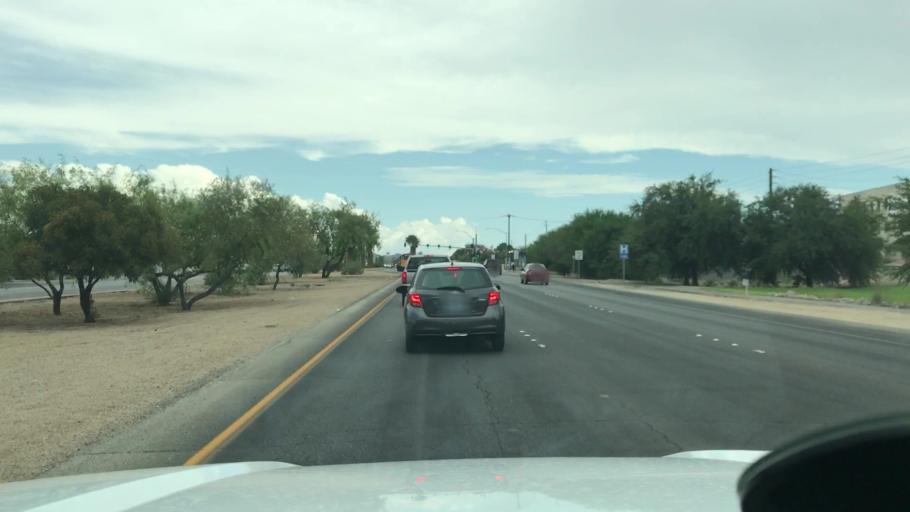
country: US
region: Nevada
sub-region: Clark County
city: Henderson
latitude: 36.0412
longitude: -114.9840
